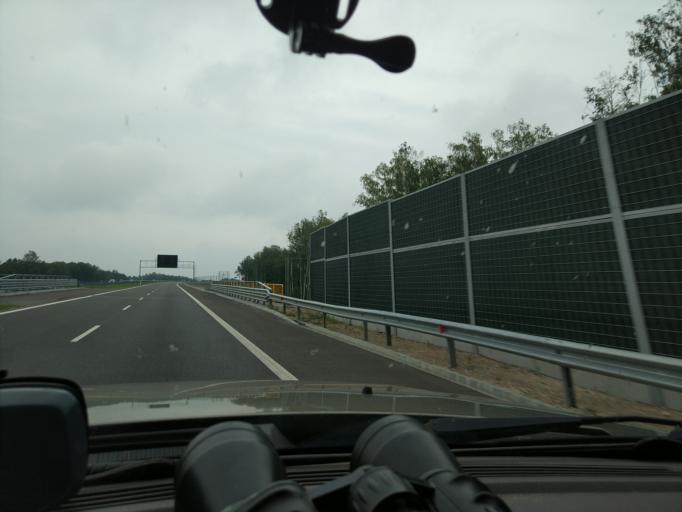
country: PL
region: Podlasie
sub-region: Powiat zambrowski
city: Szumowo
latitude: 52.9382
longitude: 22.1448
